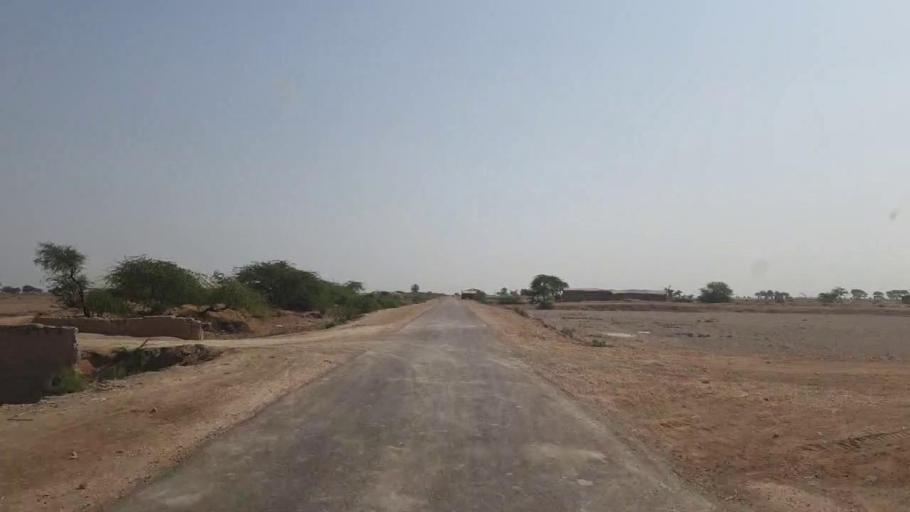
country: PK
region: Sindh
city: Jati
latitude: 24.4603
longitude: 68.5120
